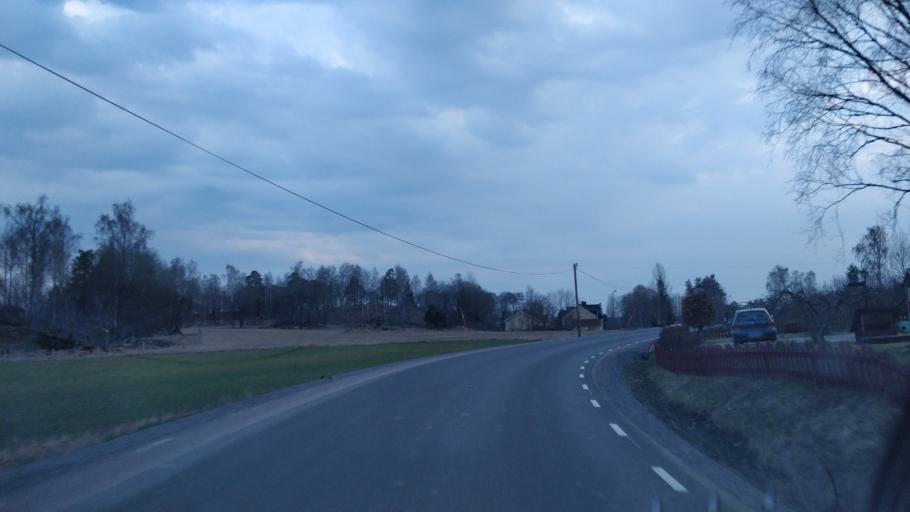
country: SE
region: Uppsala
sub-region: Enkopings Kommun
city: Orsundsbro
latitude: 59.7243
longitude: 17.2714
